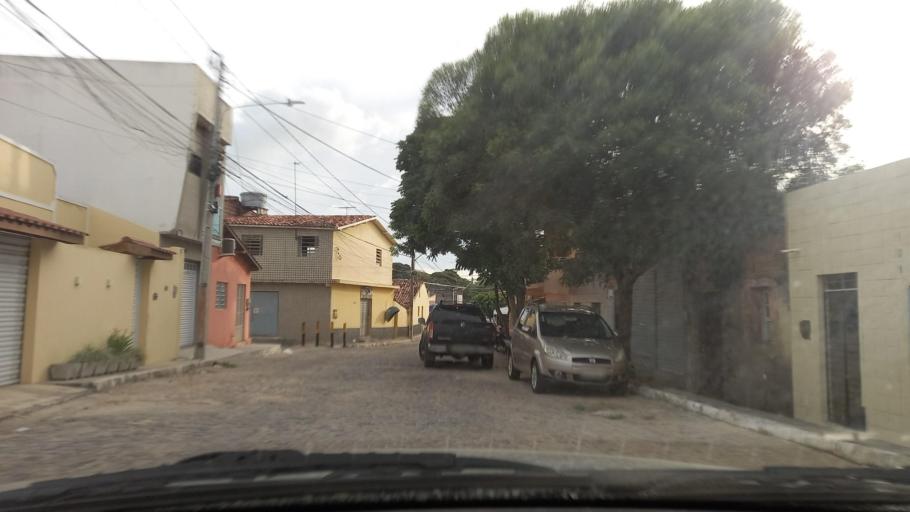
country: BR
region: Pernambuco
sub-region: Gravata
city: Gravata
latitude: -8.2034
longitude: -35.5644
